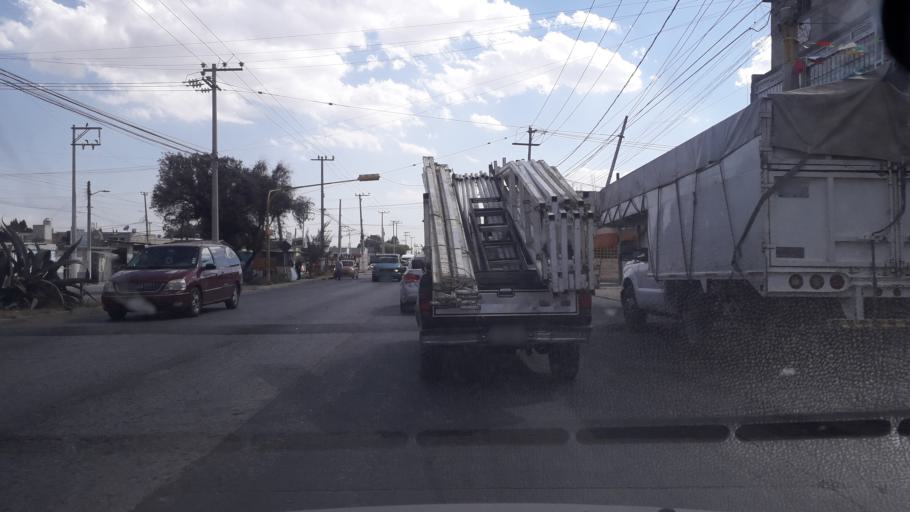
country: MX
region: Mexico
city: Ecatepec
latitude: 19.6363
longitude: -99.0557
